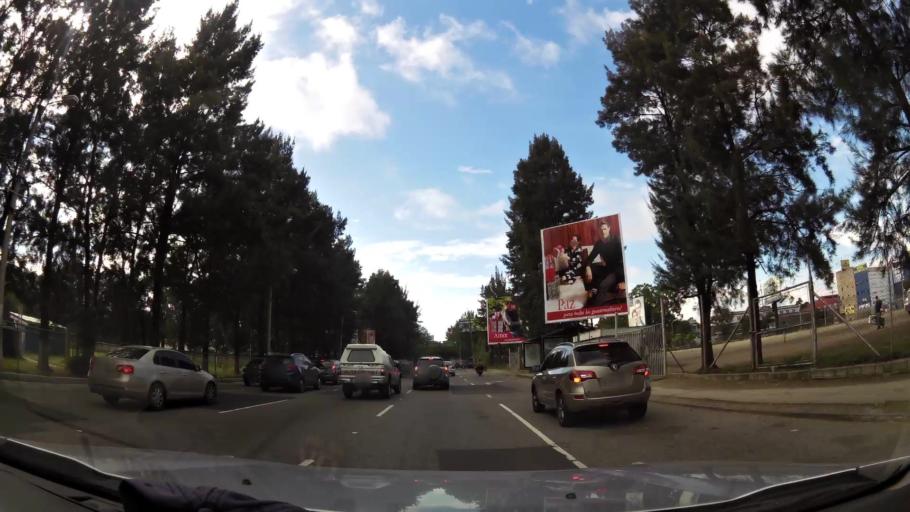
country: GT
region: Guatemala
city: Guatemala City
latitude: 14.6142
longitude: -90.5093
